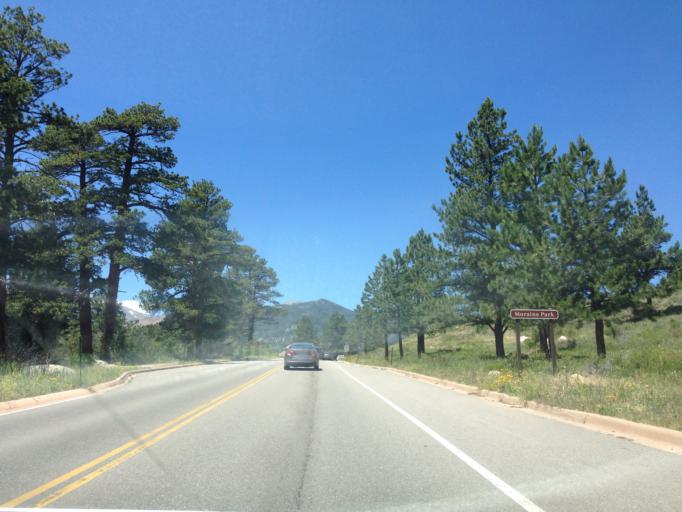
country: US
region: Colorado
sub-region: Larimer County
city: Estes Park
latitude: 40.3515
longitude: -105.5791
